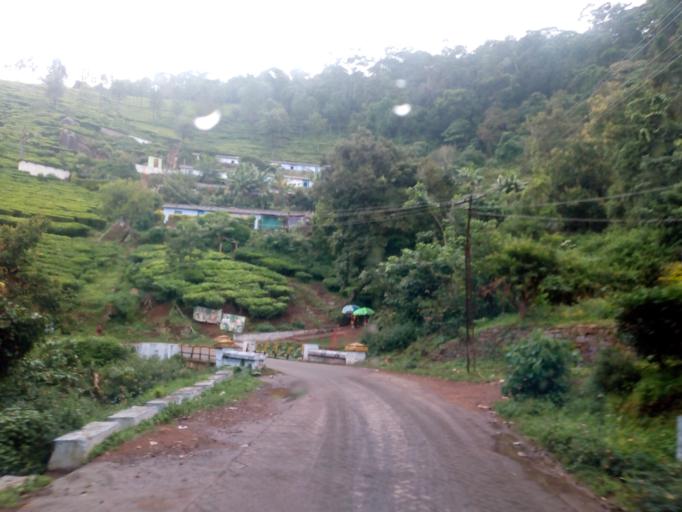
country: IN
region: Tamil Nadu
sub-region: Nilgiri
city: Wellington
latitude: 11.3590
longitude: 76.8326
